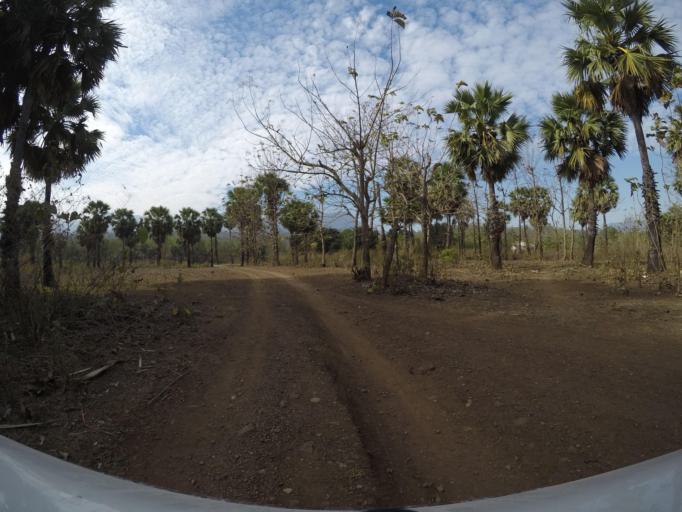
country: TL
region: Bobonaro
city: Maliana
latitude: -8.9933
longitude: 125.2051
